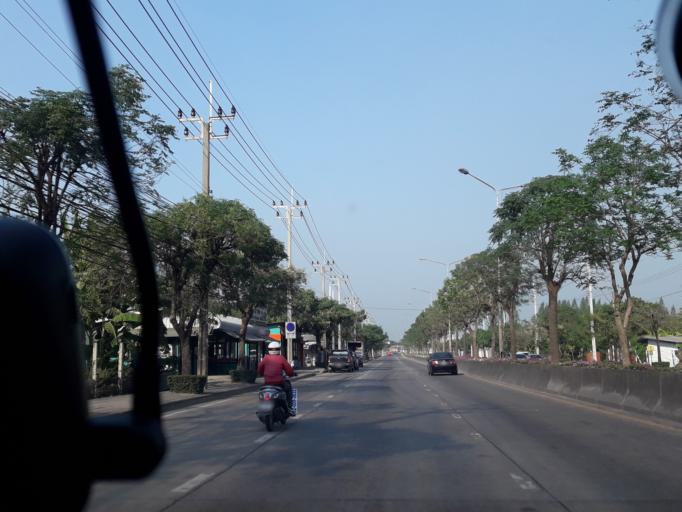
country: TH
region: Pathum Thani
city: Lam Luk Ka
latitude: 13.8950
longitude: 100.7329
